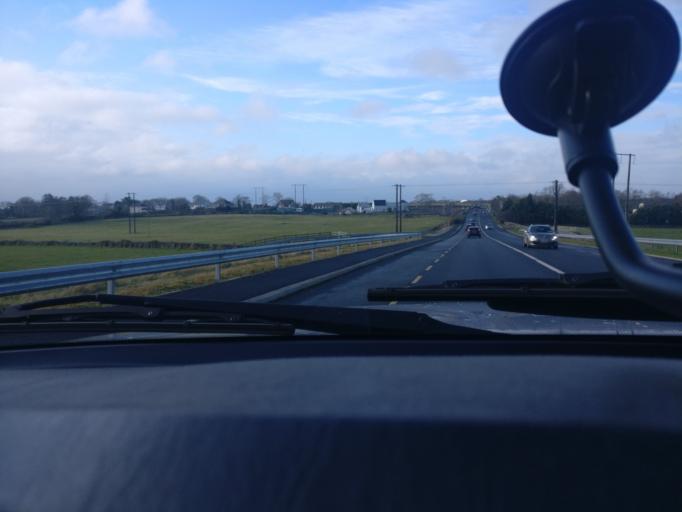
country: IE
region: Connaught
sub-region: County Galway
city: Athenry
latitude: 53.2638
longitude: -8.8183
